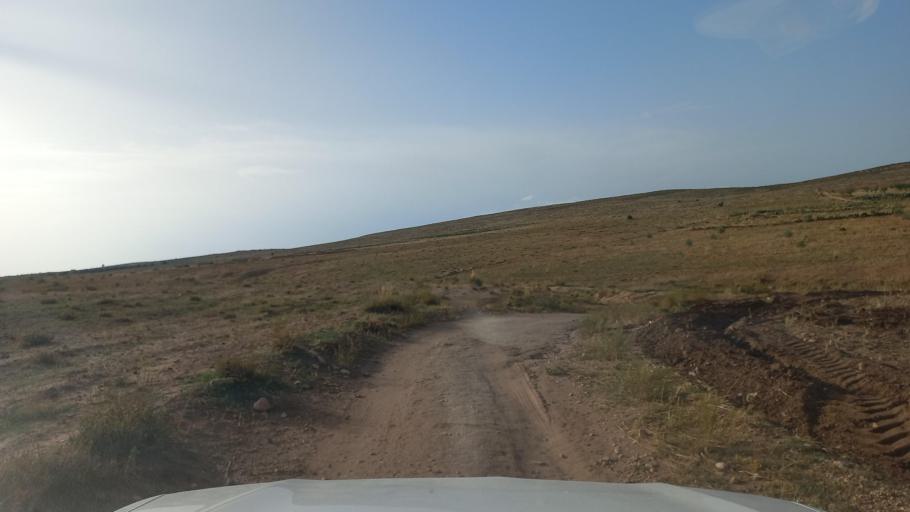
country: TN
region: Al Qasrayn
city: Kasserine
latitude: 35.3571
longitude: 8.8418
